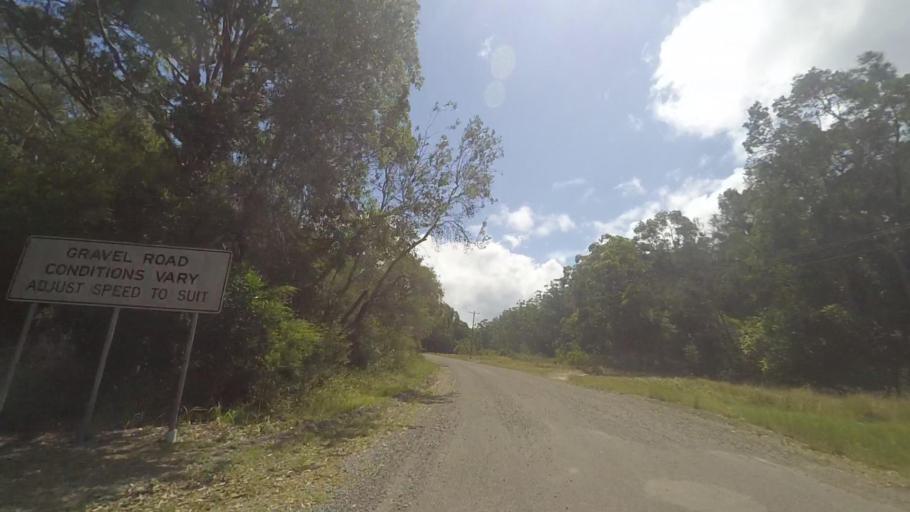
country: AU
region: New South Wales
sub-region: Great Lakes
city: Bulahdelah
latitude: -32.5089
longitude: 152.2968
